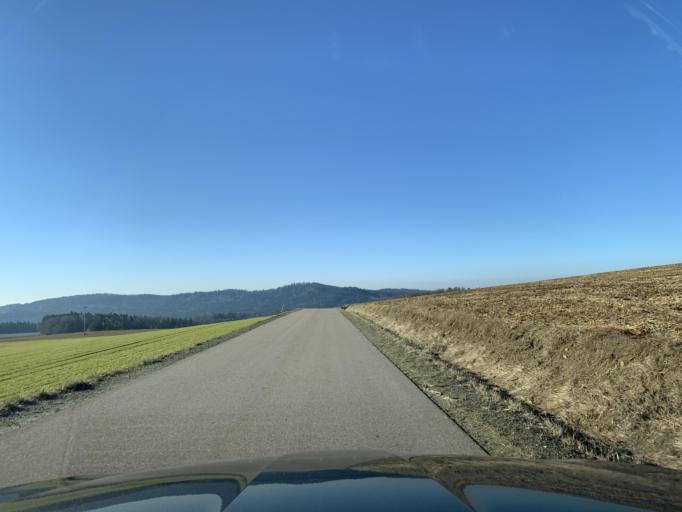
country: DE
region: Bavaria
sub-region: Upper Palatinate
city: Winklarn
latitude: 49.4126
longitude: 12.4513
